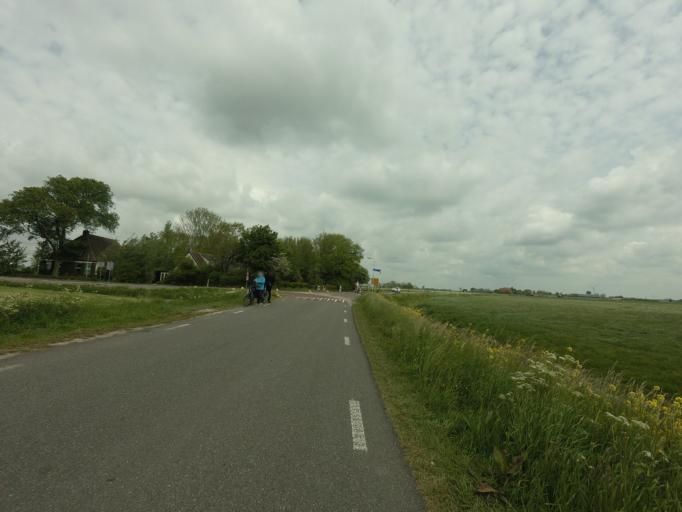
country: NL
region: Friesland
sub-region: Sudwest Fryslan
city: Bolsward
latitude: 53.1051
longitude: 5.5427
